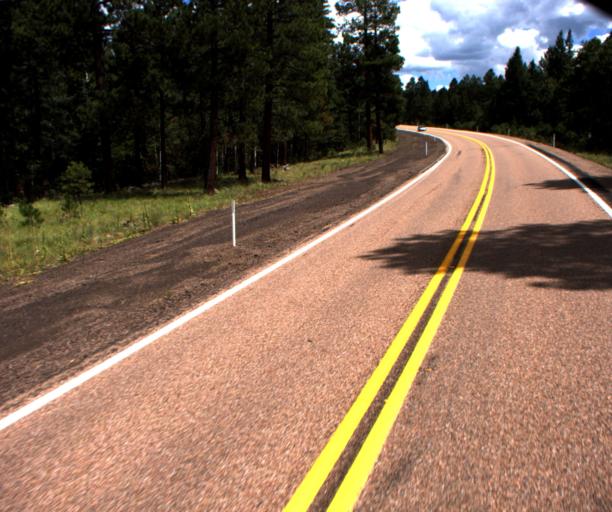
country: US
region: Arizona
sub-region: Navajo County
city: Pinetop-Lakeside
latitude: 34.0245
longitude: -109.6497
